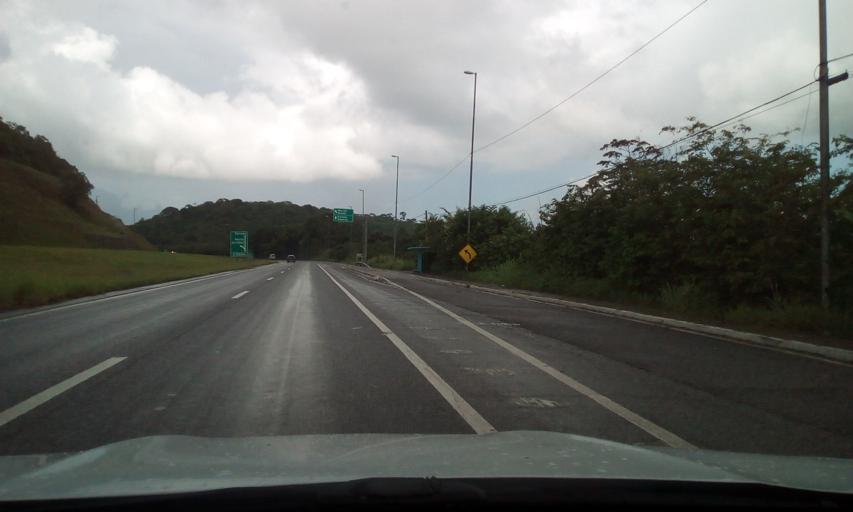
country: BR
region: Pernambuco
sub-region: Cabo De Santo Agostinho
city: Cabo
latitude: -8.3081
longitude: -35.0753
